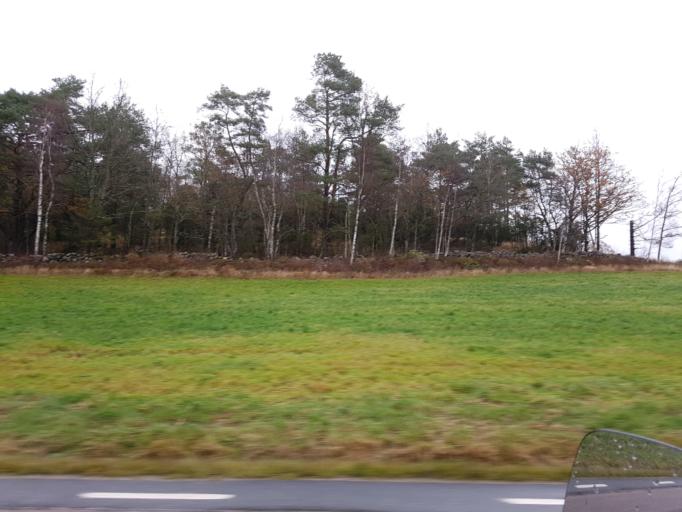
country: SE
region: Vaestra Goetaland
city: Svanesund
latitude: 58.1526
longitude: 11.7987
